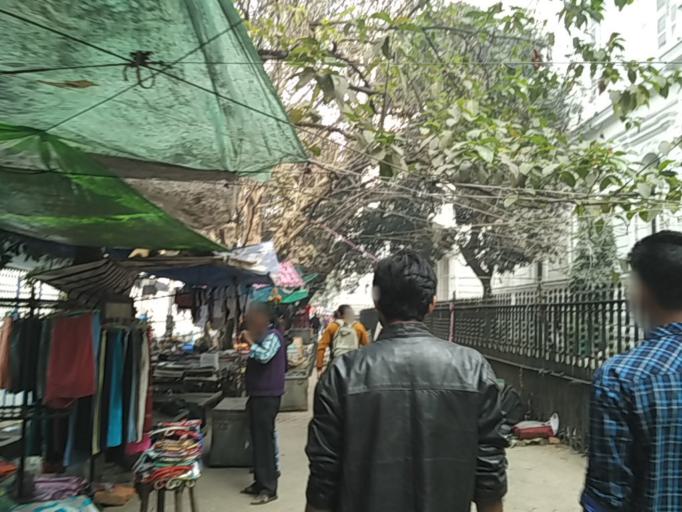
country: IN
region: West Bengal
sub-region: Kolkata
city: Bara Bazar
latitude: 22.5575
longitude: 88.3506
